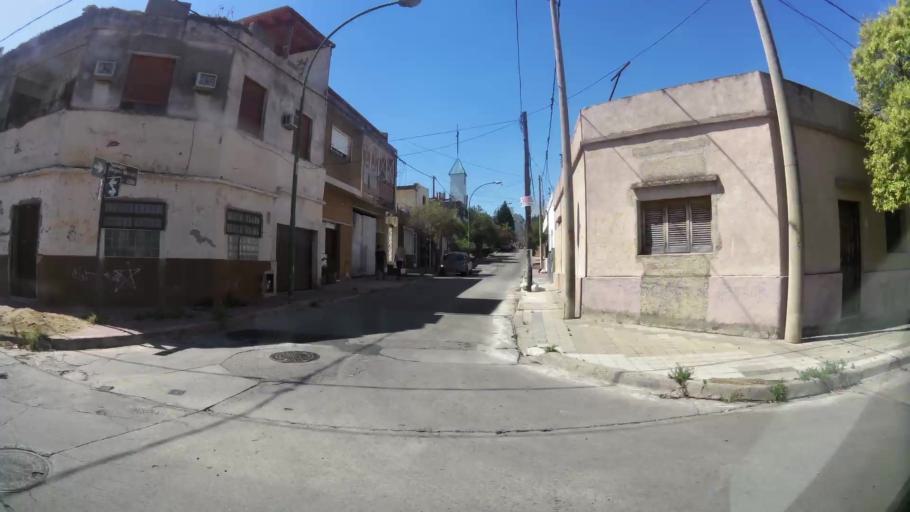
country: AR
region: Cordoba
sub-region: Departamento de Capital
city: Cordoba
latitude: -31.4041
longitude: -64.1793
